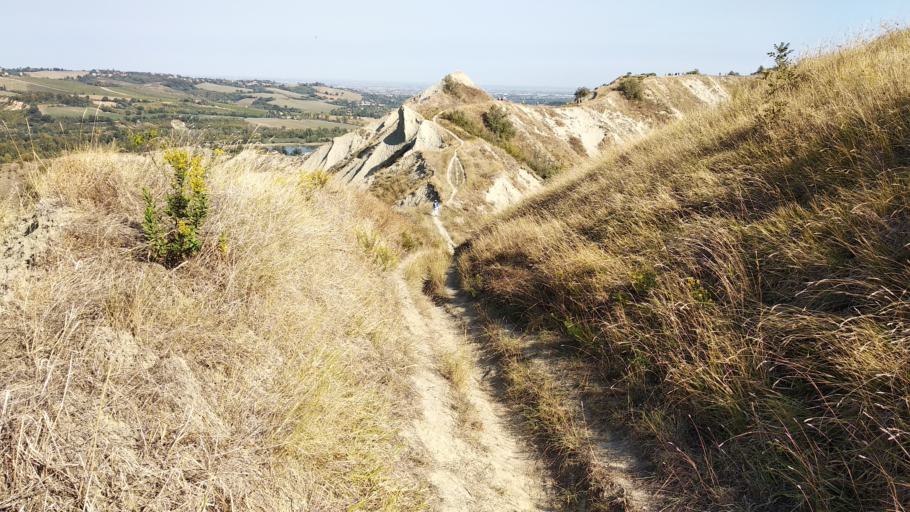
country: IT
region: Emilia-Romagna
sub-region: Provincia di Bologna
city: Castel San Pietro Terme
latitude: 44.3447
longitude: 11.5766
